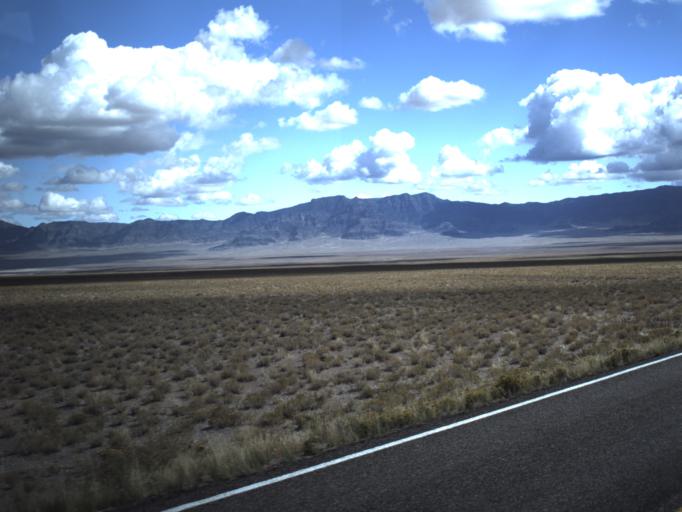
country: US
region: Utah
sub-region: Beaver County
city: Milford
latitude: 38.5729
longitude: -113.7918
